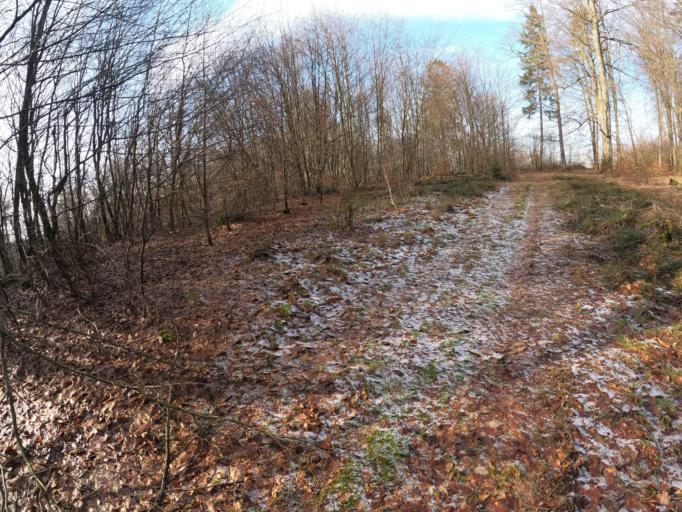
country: PL
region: West Pomeranian Voivodeship
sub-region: Powiat koszalinski
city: Polanow
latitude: 54.1216
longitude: 16.7002
